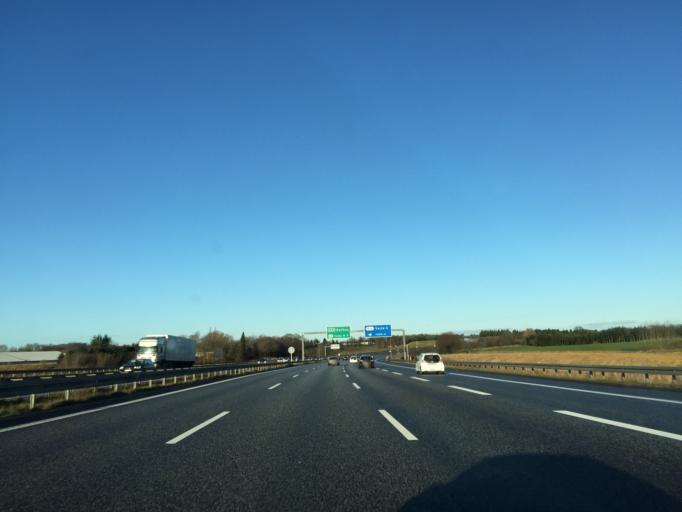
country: DK
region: South Denmark
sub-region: Vejle Kommune
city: Vejle
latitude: 55.6678
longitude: 9.5538
